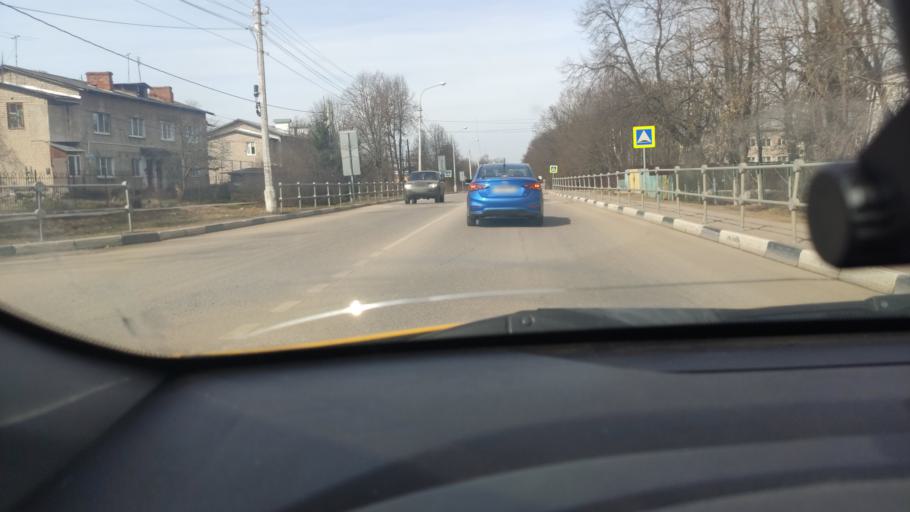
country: RU
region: Moskovskaya
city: Ruza
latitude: 55.7055
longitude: 36.1876
